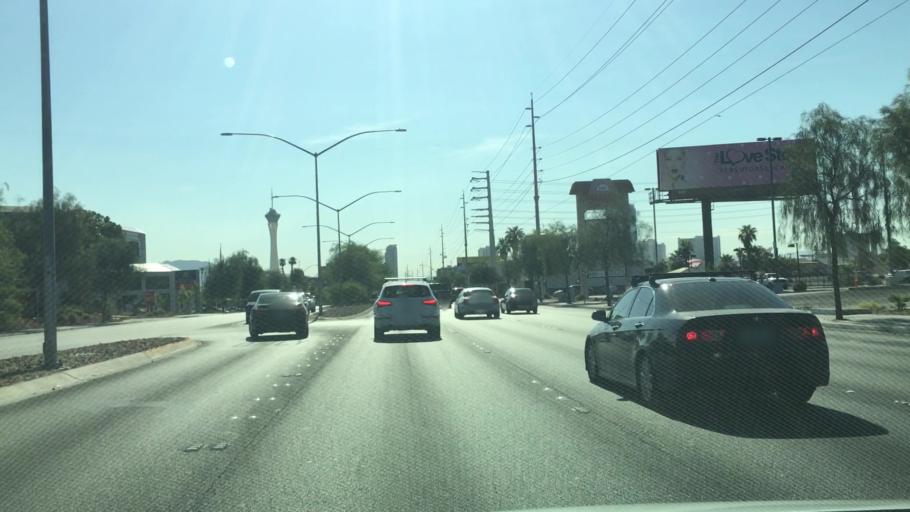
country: US
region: Nevada
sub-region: Clark County
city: Las Vegas
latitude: 36.1443
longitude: -115.1885
